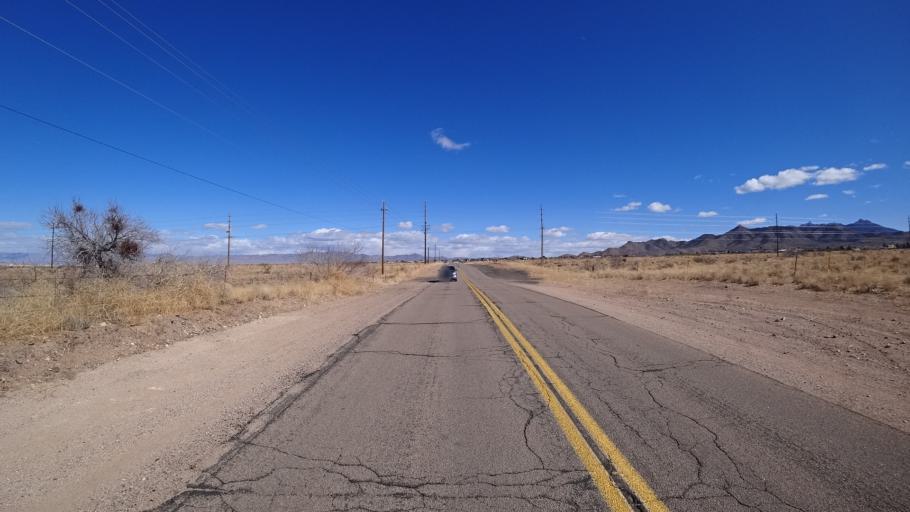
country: US
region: Arizona
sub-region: Mohave County
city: Kingman
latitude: 35.1999
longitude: -113.9900
